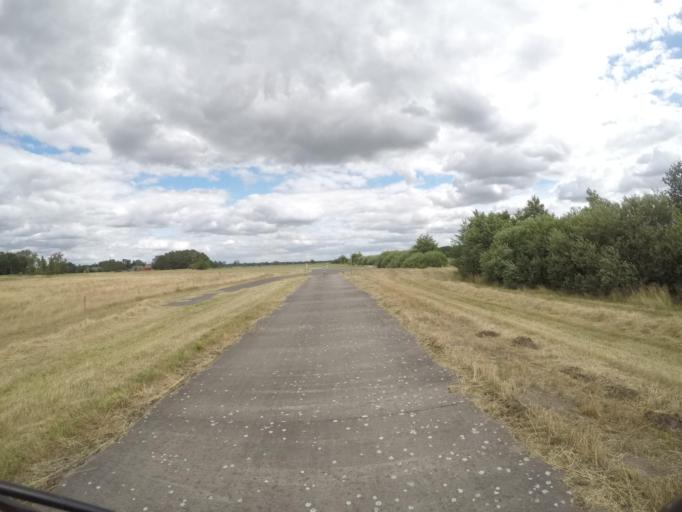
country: DE
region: Mecklenburg-Vorpommern
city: Lubtheen
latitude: 53.2912
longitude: 10.9969
